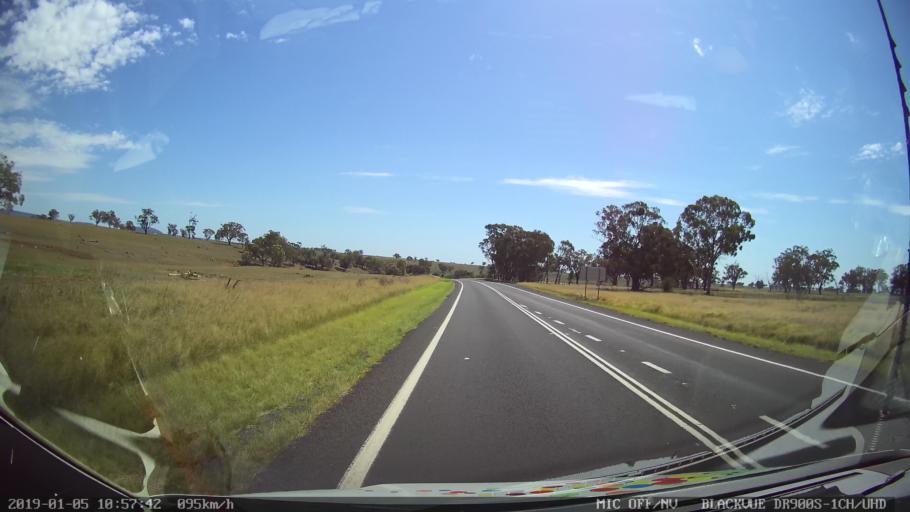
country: AU
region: New South Wales
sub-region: Warrumbungle Shire
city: Coonabarabran
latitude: -31.4290
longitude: 149.1732
